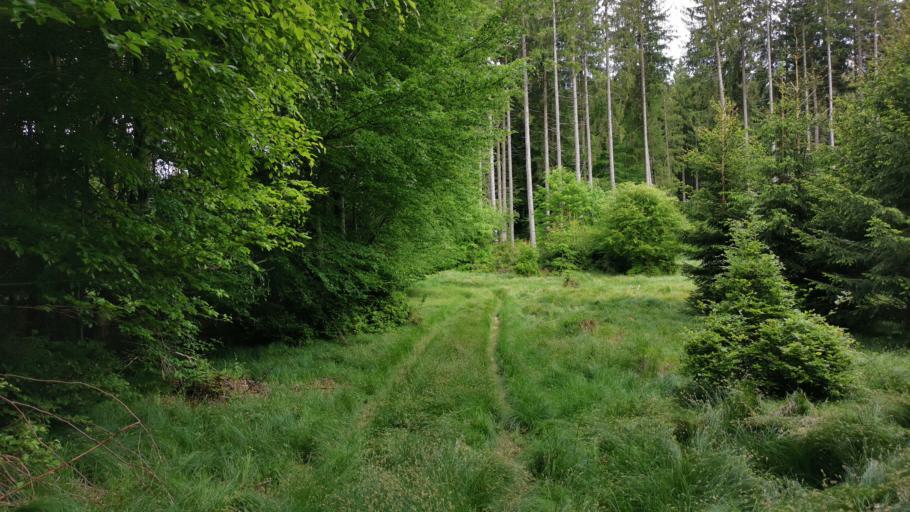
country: DE
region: Bavaria
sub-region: Upper Bavaria
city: Baierbrunn
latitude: 48.0262
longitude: 11.4609
